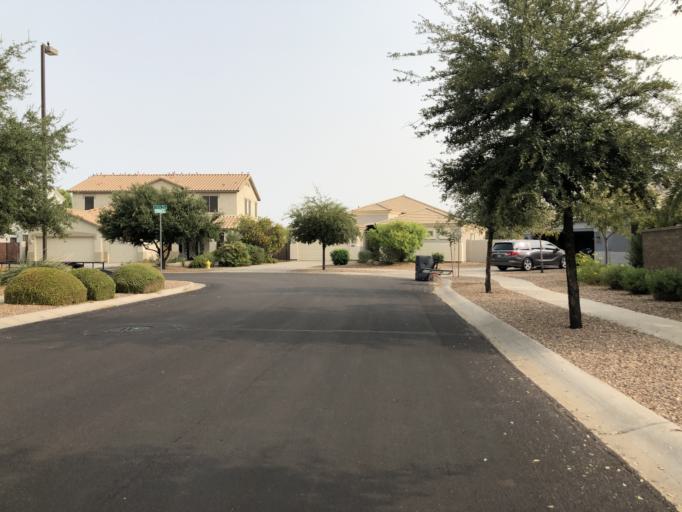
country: US
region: Arizona
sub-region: Maricopa County
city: Queen Creek
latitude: 33.2756
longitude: -111.6949
